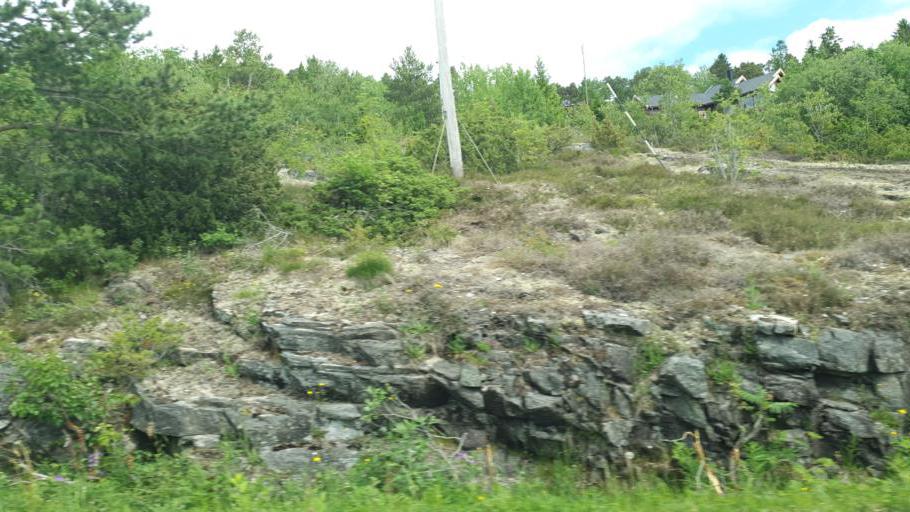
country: NO
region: Sor-Trondelag
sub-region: Trondheim
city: Trondheim
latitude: 63.5726
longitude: 10.3975
